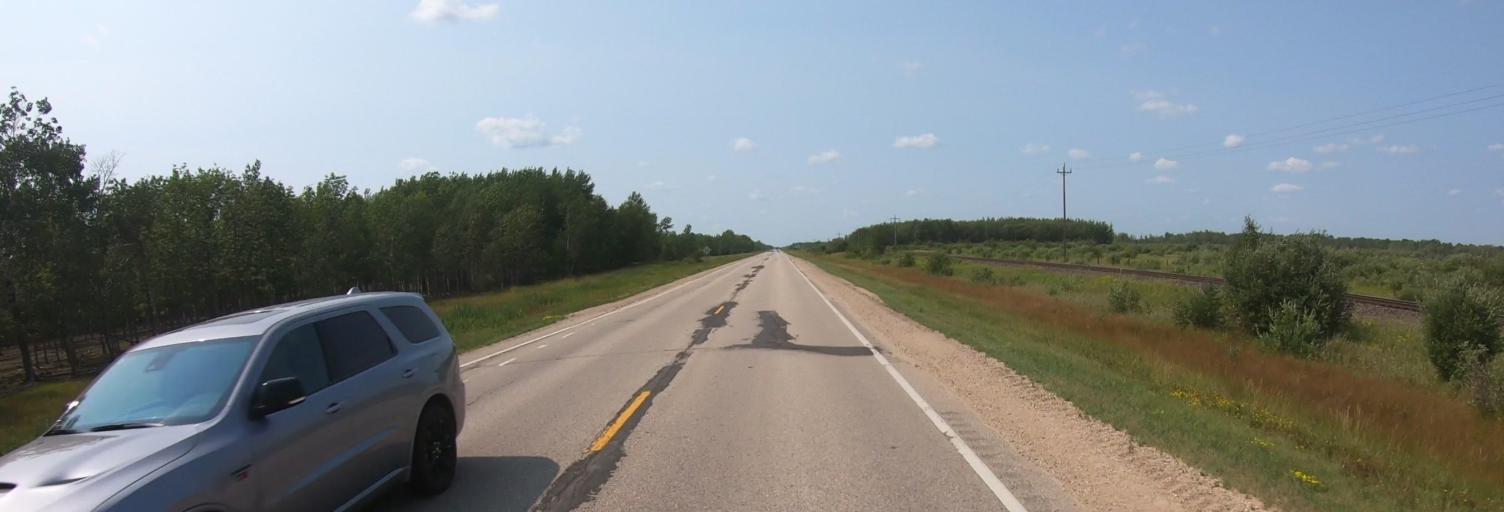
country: US
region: Minnesota
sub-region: Lake of the Woods County
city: Baudette
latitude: 48.7485
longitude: -94.8732
